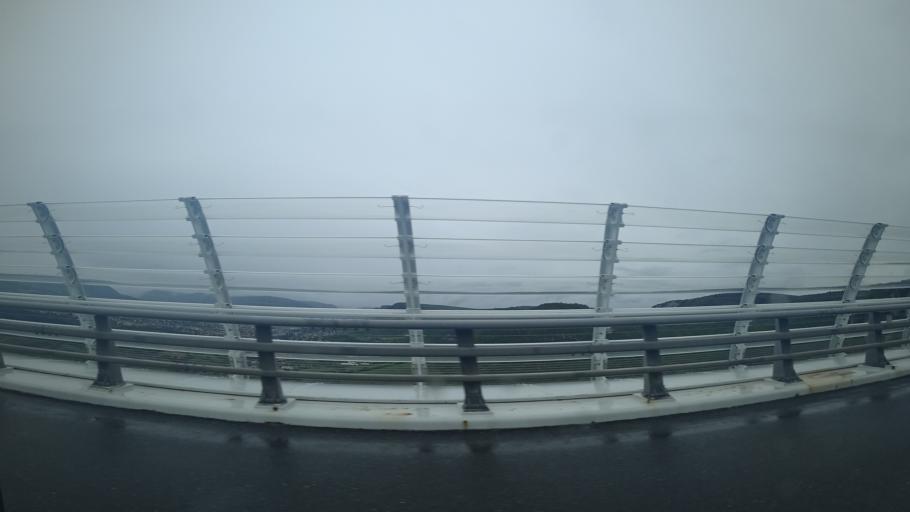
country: FR
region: Midi-Pyrenees
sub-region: Departement de l'Aveyron
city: Saint-Georges-de-Luzencon
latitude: 44.0730
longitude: 3.0238
